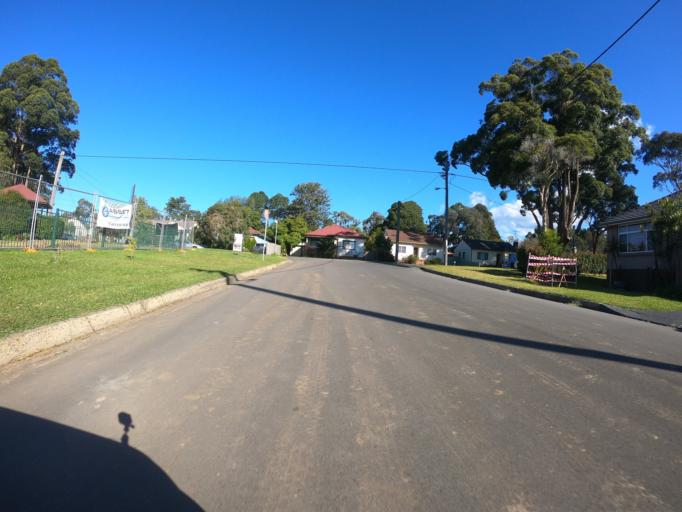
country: AU
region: New South Wales
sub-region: Wollongong
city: East Corrimal
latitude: -34.3604
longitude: 150.9037
